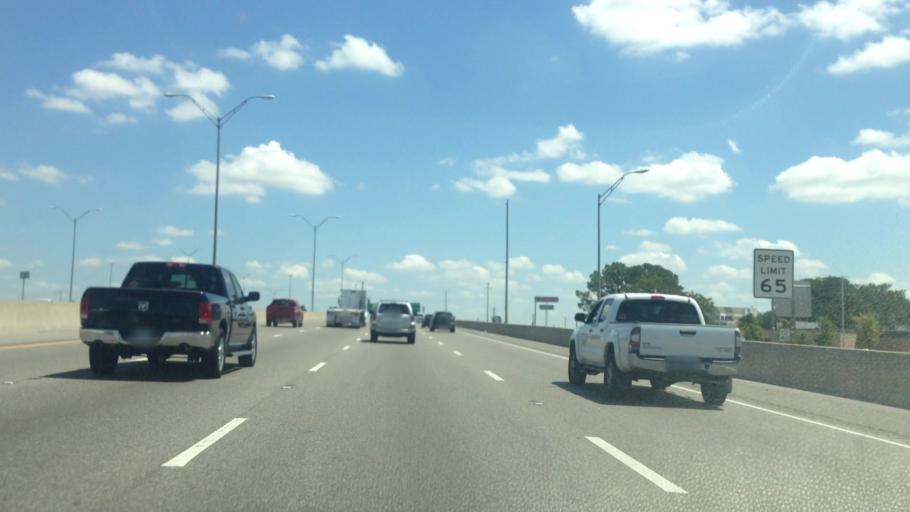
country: US
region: Texas
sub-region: Tarrant County
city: Bedford
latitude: 32.8365
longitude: -97.1369
